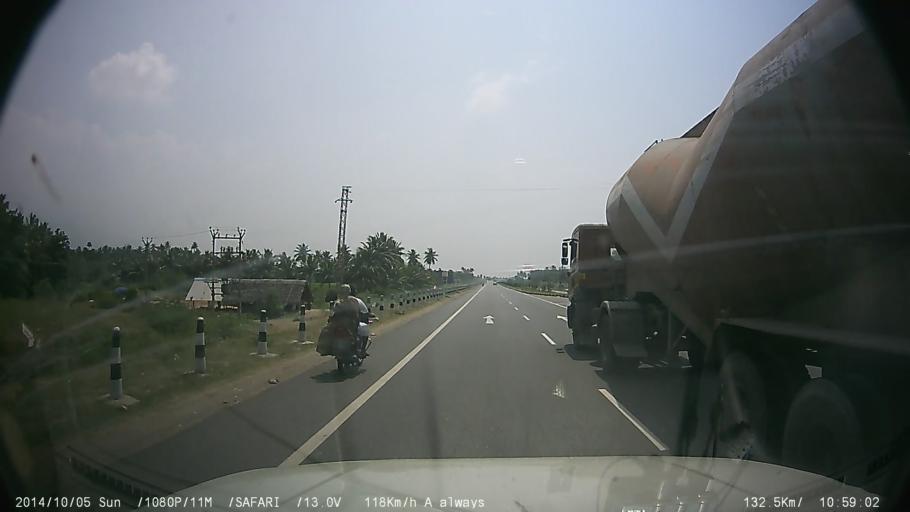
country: IN
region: Tamil Nadu
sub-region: Salem
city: Attur
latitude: 11.6387
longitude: 78.5245
